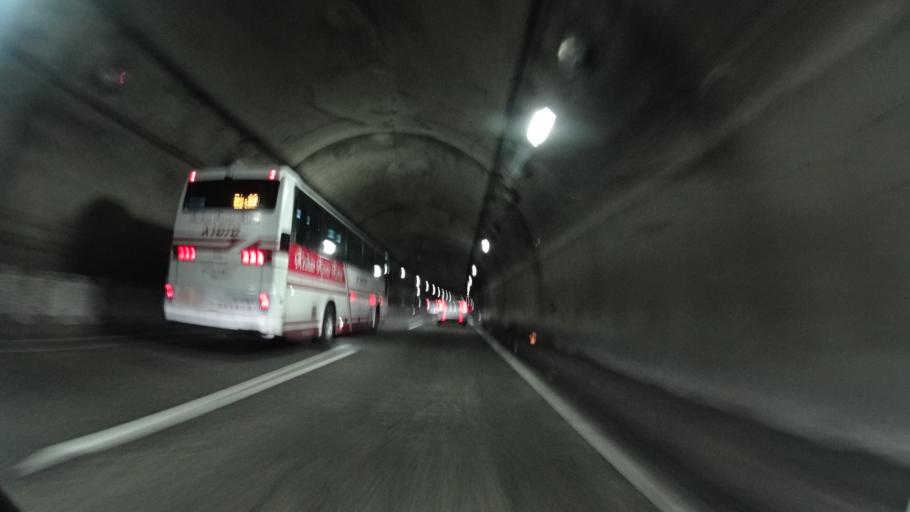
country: JP
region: Okayama
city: Okayama-shi
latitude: 34.7266
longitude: 133.9667
